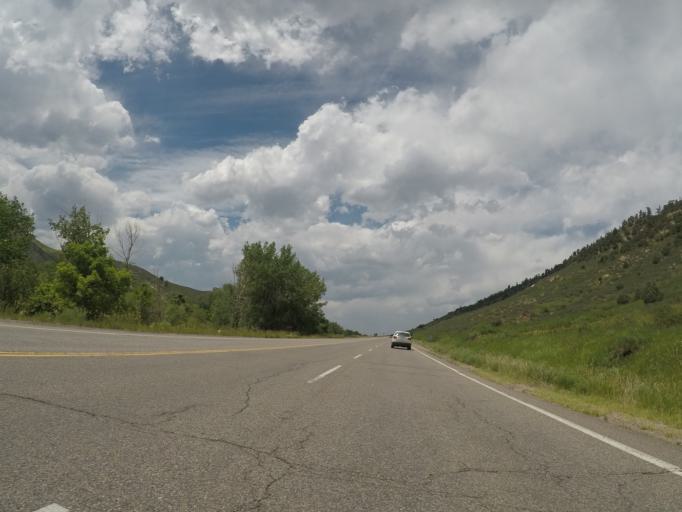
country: US
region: Colorado
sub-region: Jefferson County
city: West Pleasant View
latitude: 39.6830
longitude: -105.1987
